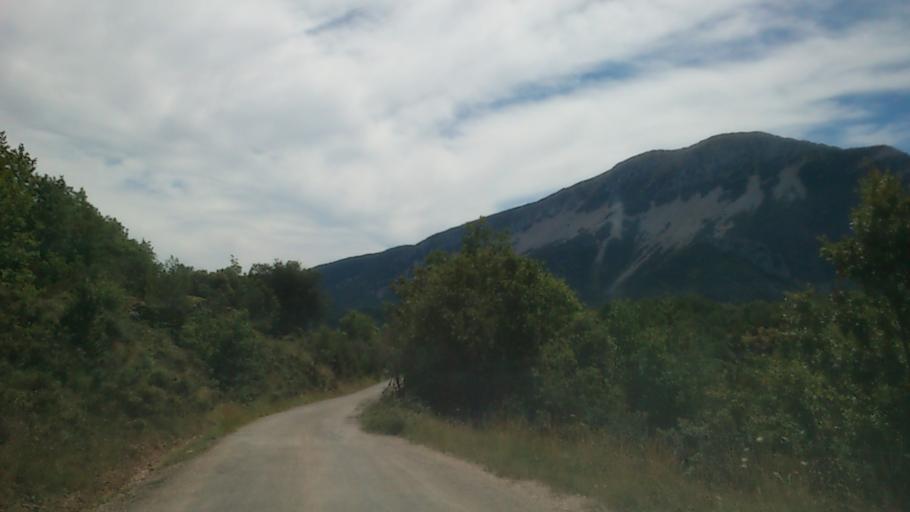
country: ES
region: Aragon
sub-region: Provincia de Huesca
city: Loporzano
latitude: 42.3177
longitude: -0.2713
